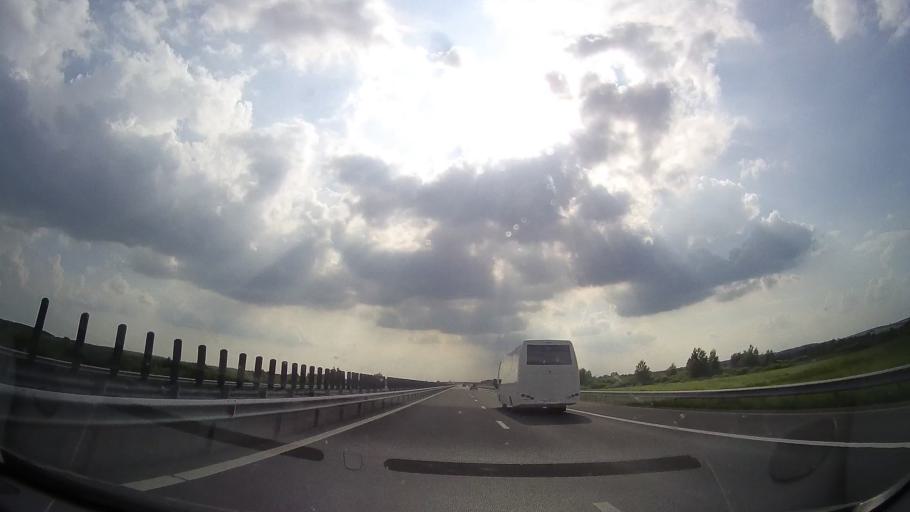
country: RO
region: Timis
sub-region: Comuna Bethausen
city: Bethausen
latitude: 45.8091
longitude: 21.9323
